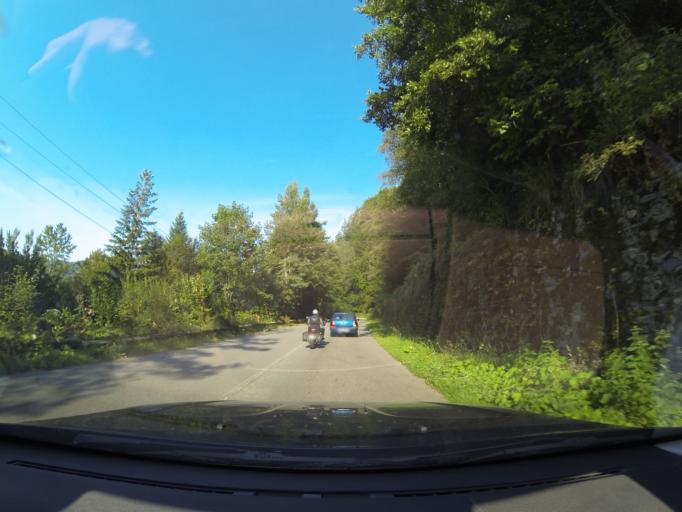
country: RO
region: Arges
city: Poenari
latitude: 45.3684
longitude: 24.6534
